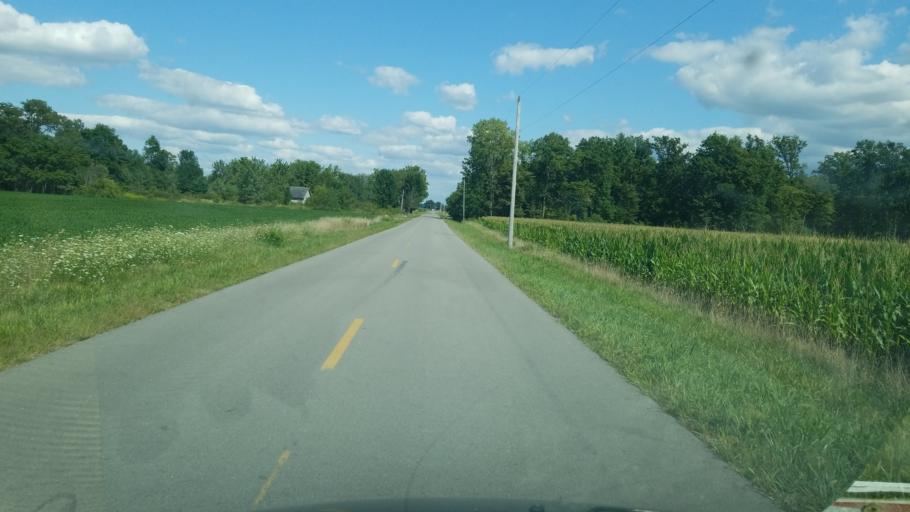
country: US
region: Ohio
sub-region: Logan County
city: Lakeview
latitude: 40.5135
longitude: -83.9432
